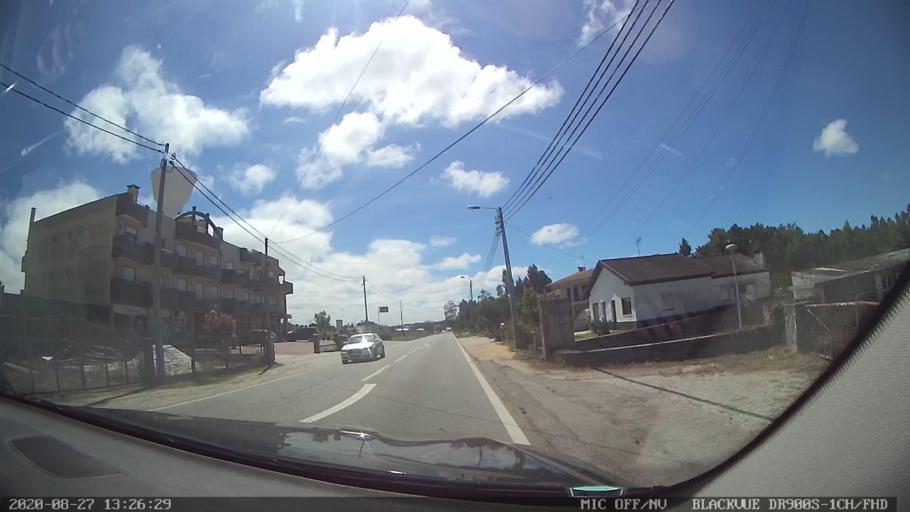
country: PT
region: Aveiro
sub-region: Vagos
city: Vagos
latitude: 40.5373
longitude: -8.6767
